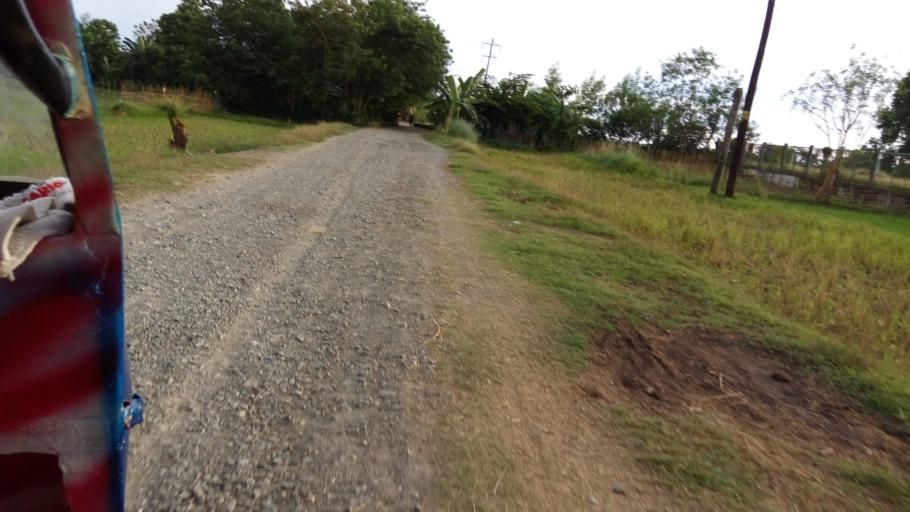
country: PH
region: Ilocos
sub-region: Province of La Union
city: Santo Tomas
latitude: 16.2823
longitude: 120.3846
